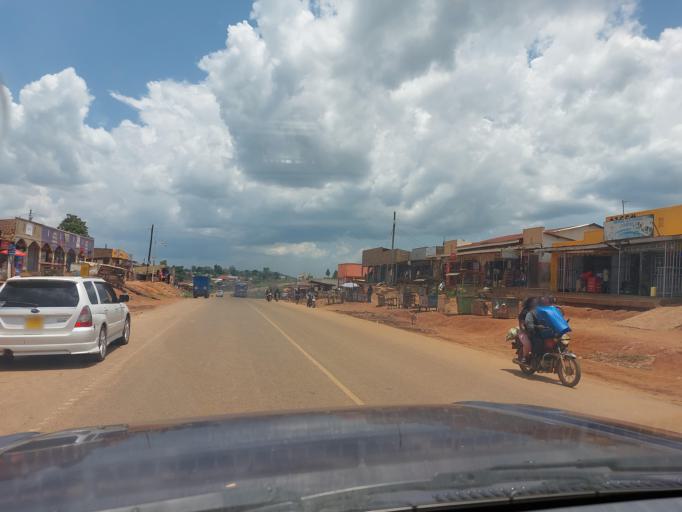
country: UG
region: Central Region
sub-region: Mukono District
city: Mukono
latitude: 0.3010
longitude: 32.7786
